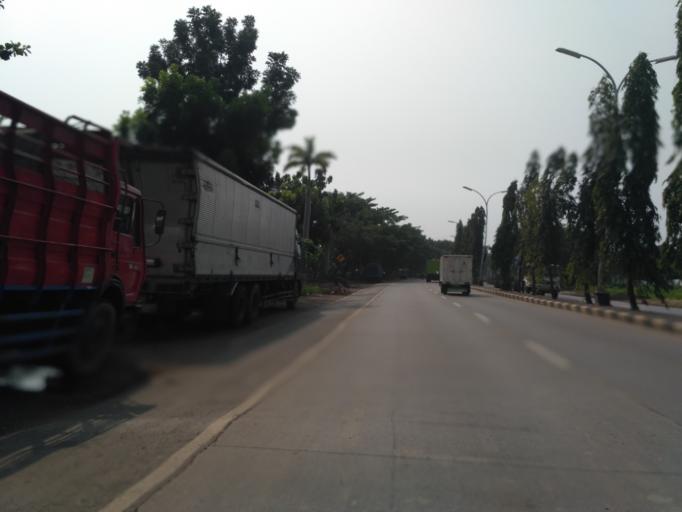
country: ID
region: Central Java
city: Semarang
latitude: -6.9764
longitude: 110.3875
